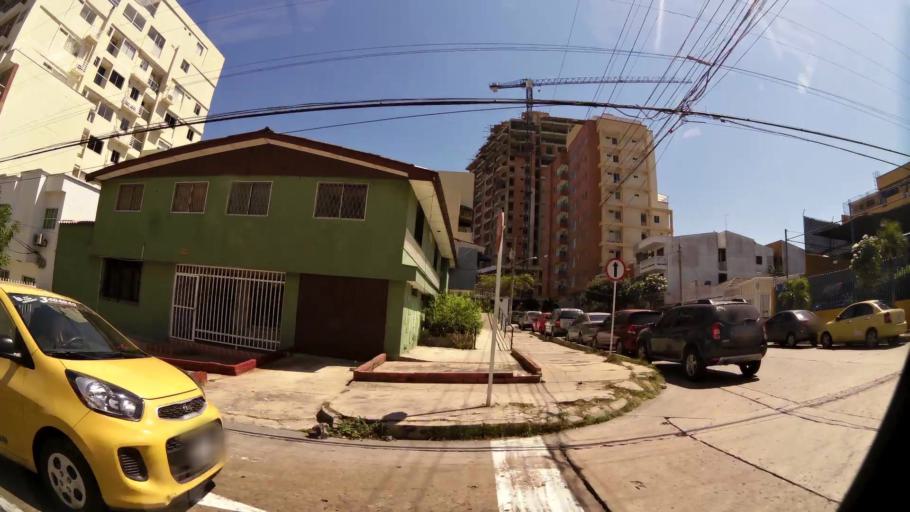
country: CO
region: Atlantico
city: Barranquilla
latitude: 10.9898
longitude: -74.8100
